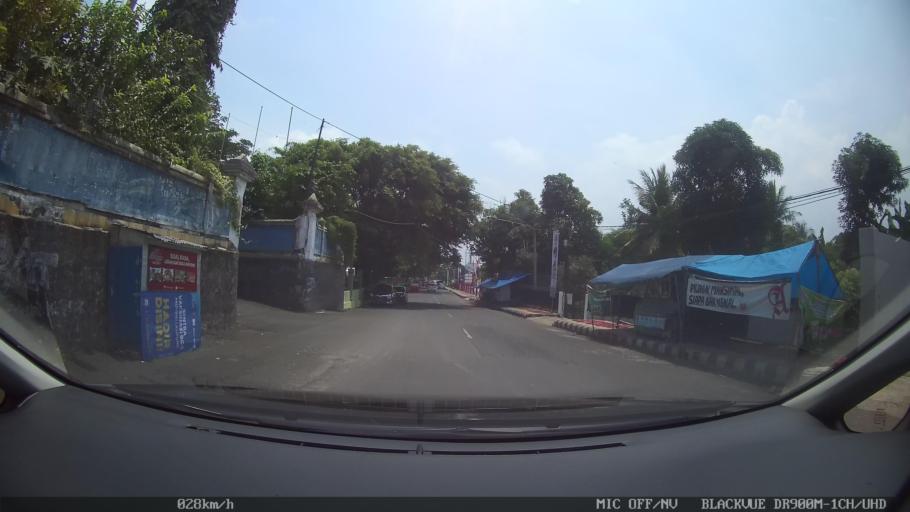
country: ID
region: Lampung
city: Bandarlampung
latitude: -5.4204
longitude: 105.2604
